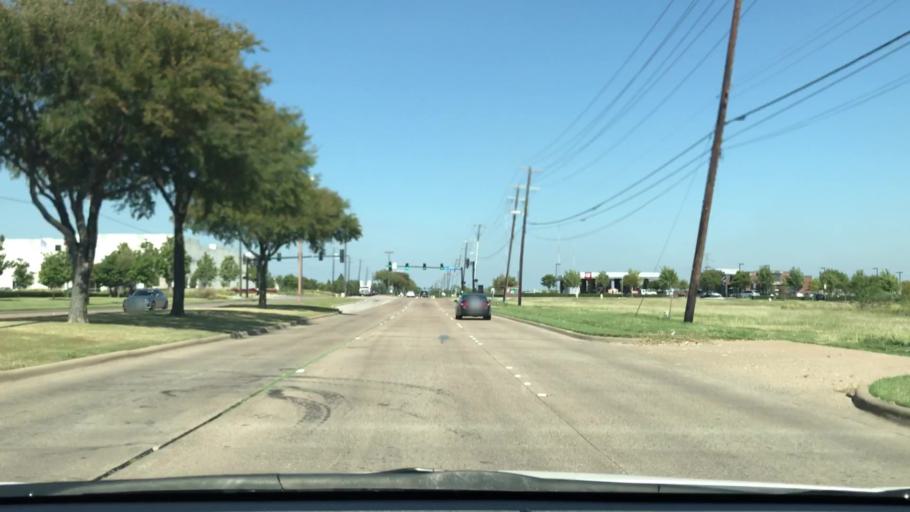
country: US
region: Texas
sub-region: Dallas County
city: Coppell
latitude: 32.9287
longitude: -96.9935
